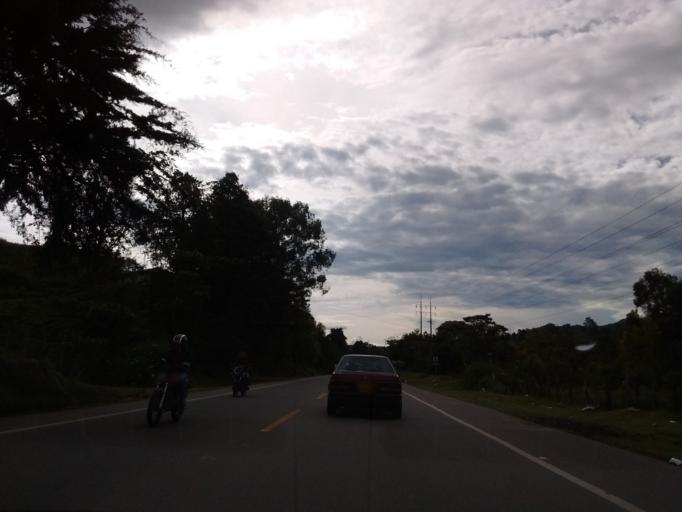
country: CO
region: Antioquia
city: Santuario
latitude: 6.1267
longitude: -75.2505
